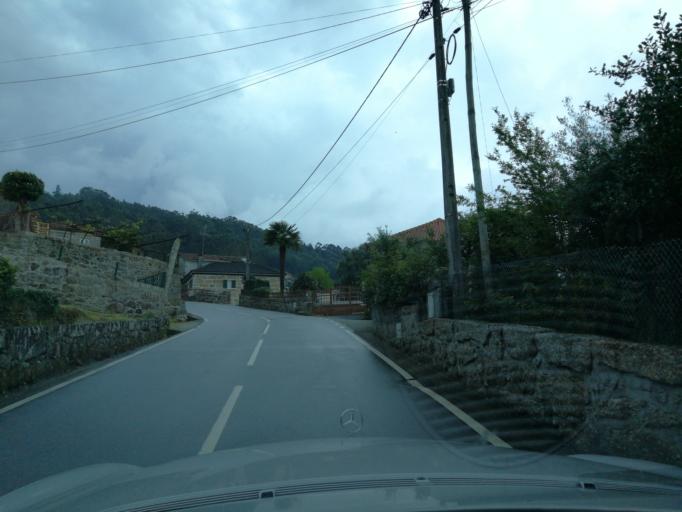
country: PT
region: Braga
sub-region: Braga
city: Oliveira
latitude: 41.4682
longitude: -8.4749
